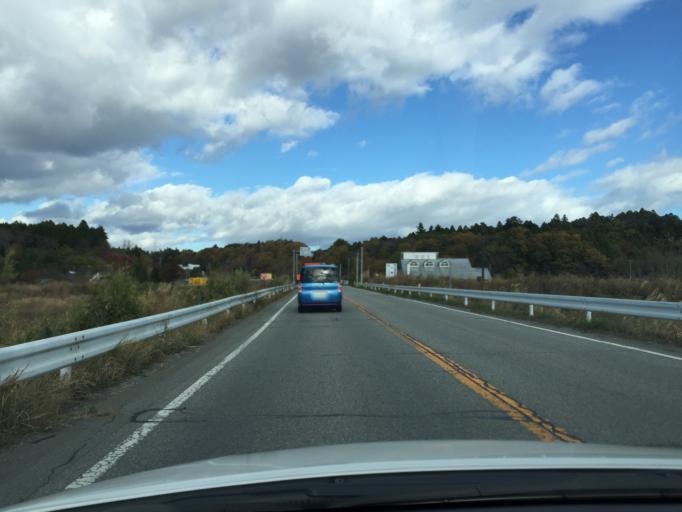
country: JP
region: Fukushima
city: Namie
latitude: 37.3874
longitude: 141.0084
